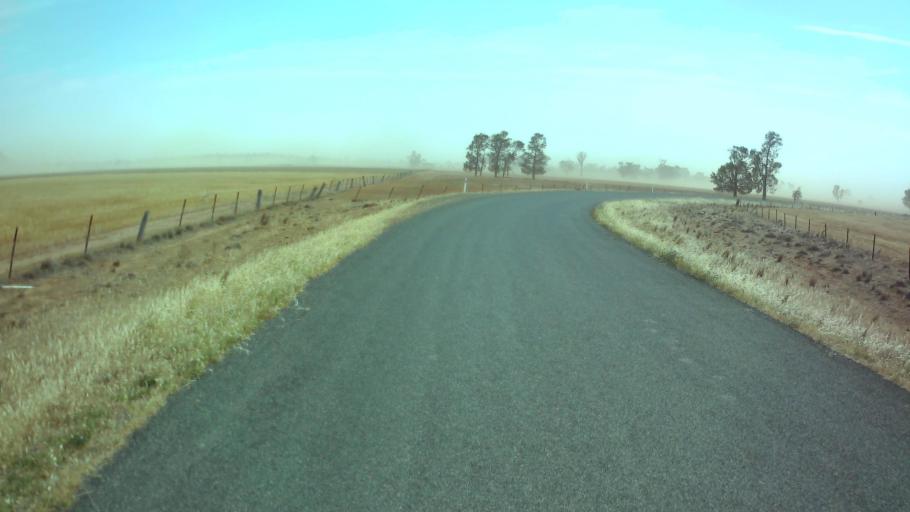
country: AU
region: New South Wales
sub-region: Weddin
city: Grenfell
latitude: -33.7383
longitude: 147.9931
